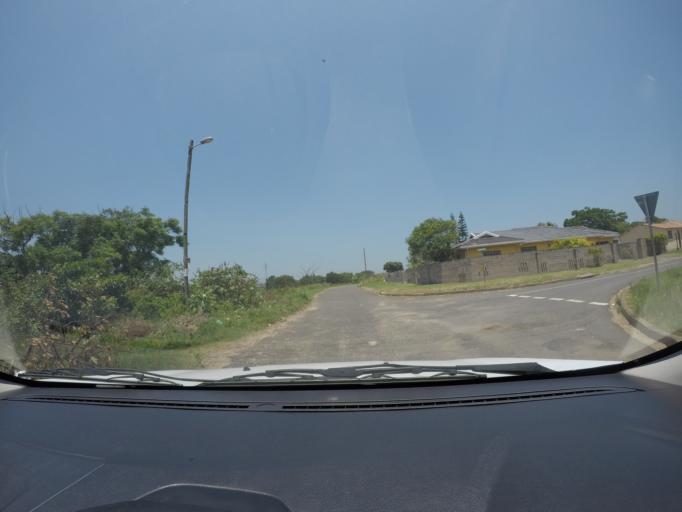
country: ZA
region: KwaZulu-Natal
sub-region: uThungulu District Municipality
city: eSikhawini
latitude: -28.8798
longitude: 31.8942
